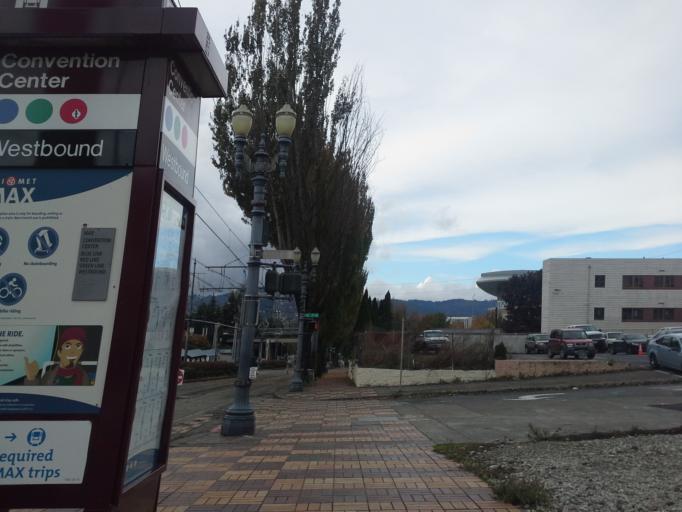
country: US
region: Oregon
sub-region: Multnomah County
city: Portland
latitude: 45.5302
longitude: -122.6625
